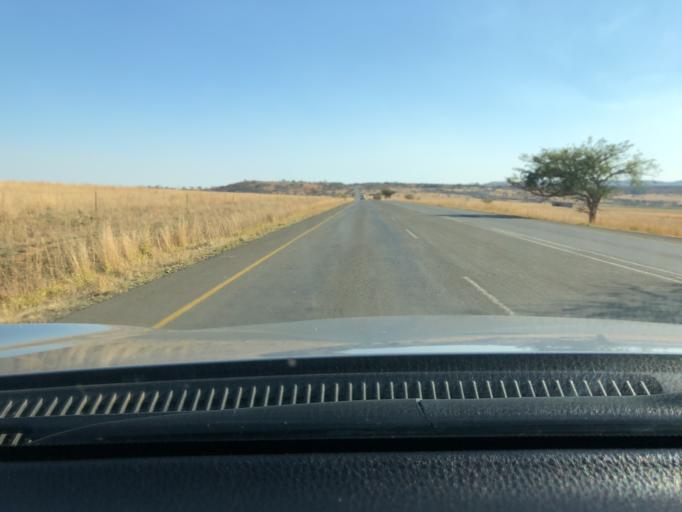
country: ZA
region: KwaZulu-Natal
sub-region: uMzinyathi District Municipality
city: Glencoe
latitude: -28.2922
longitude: 30.0759
